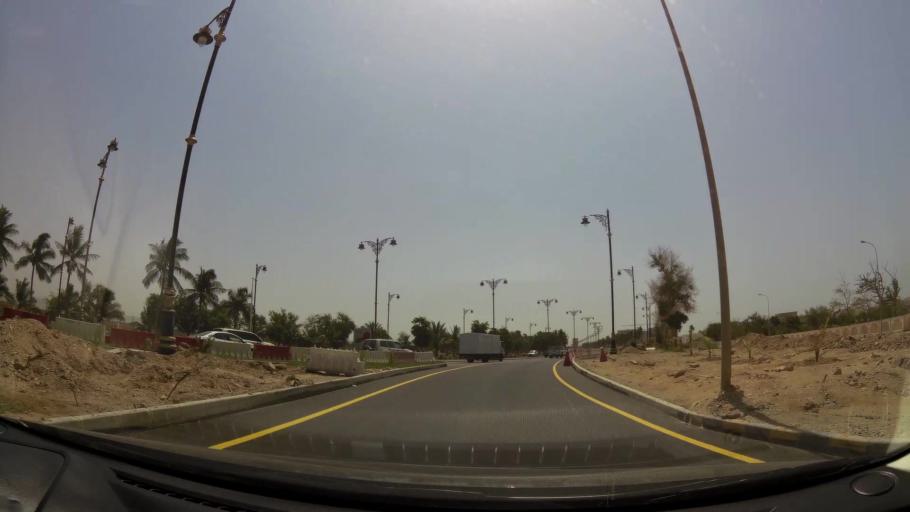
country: OM
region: Zufar
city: Salalah
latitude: 17.0231
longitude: 54.1021
